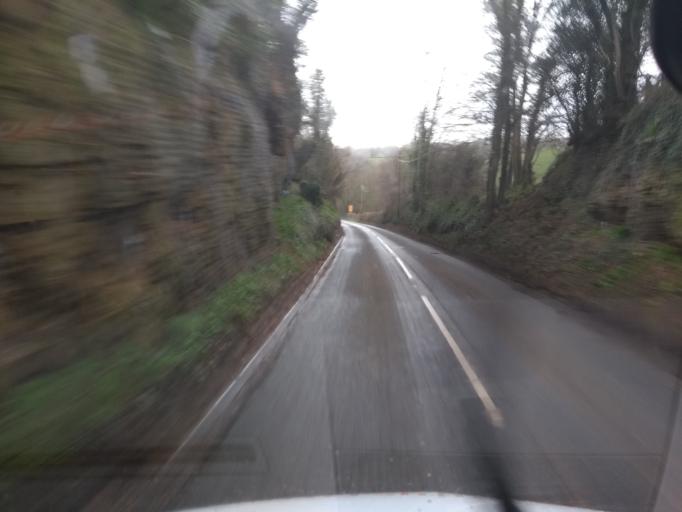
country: GB
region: England
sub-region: Somerset
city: Bruton
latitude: 51.0931
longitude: -2.4652
